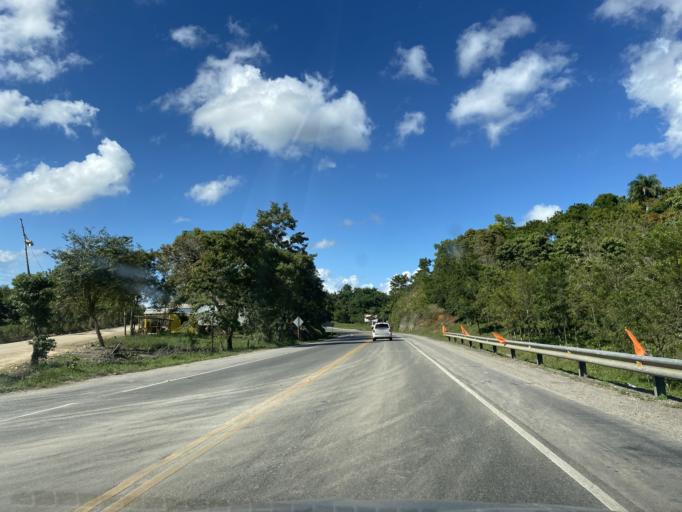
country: DO
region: Monte Plata
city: Gonzalo
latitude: 18.9626
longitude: -69.7637
